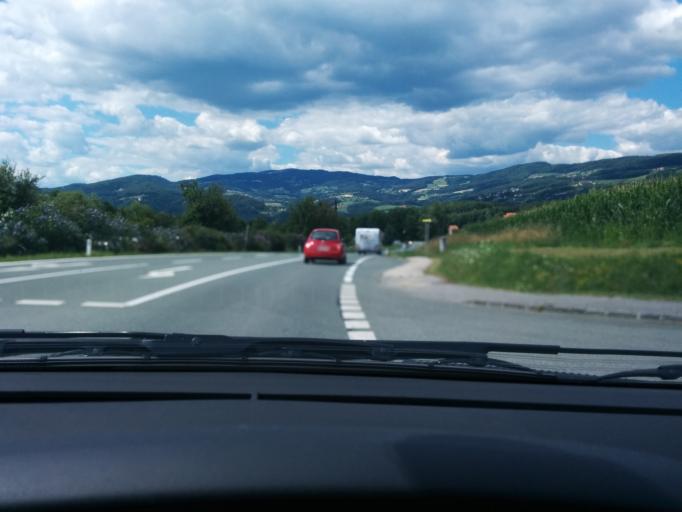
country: AT
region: Styria
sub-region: Politischer Bezirk Hartberg-Fuerstenfeld
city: Stubenberg
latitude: 47.2209
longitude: 15.8138
